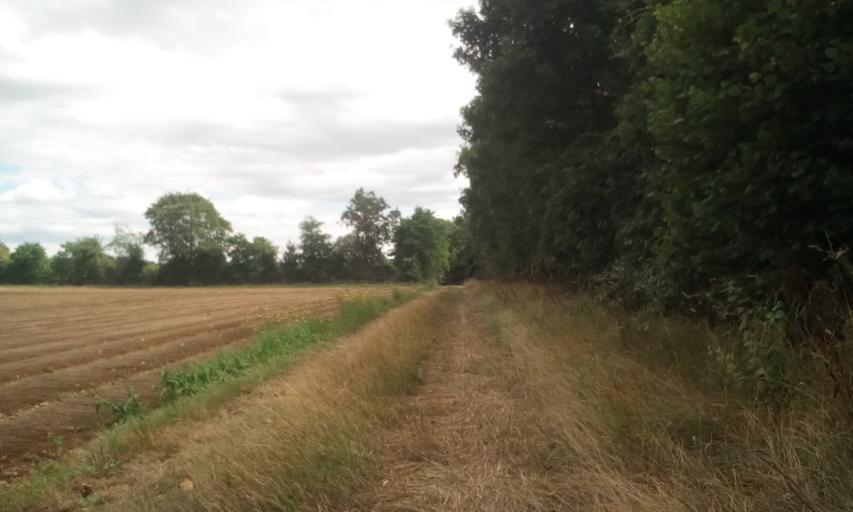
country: FR
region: Lower Normandy
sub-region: Departement du Calvados
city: Troarn
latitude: 49.1715
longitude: -0.1981
